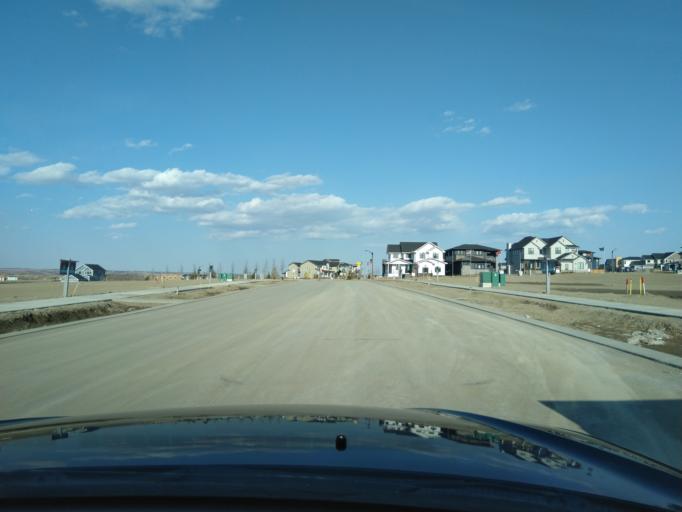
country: CA
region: Alberta
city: Cochrane
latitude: 51.1123
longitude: -114.4082
